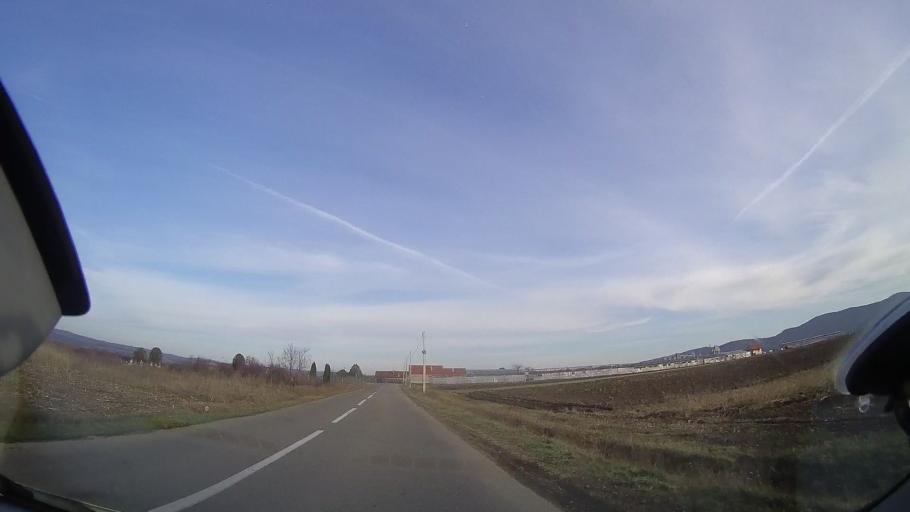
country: RO
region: Bihor
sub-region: Comuna Tetchea
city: Hotar
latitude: 47.0472
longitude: 22.3101
